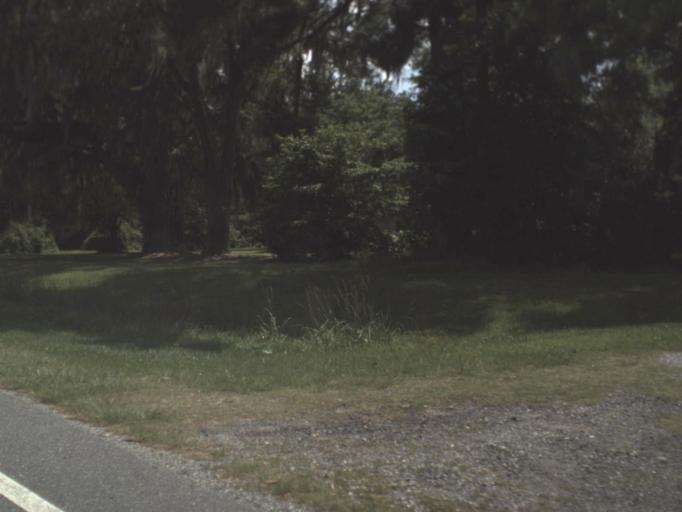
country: US
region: Florida
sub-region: Columbia County
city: Watertown
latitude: 30.0435
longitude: -82.5982
